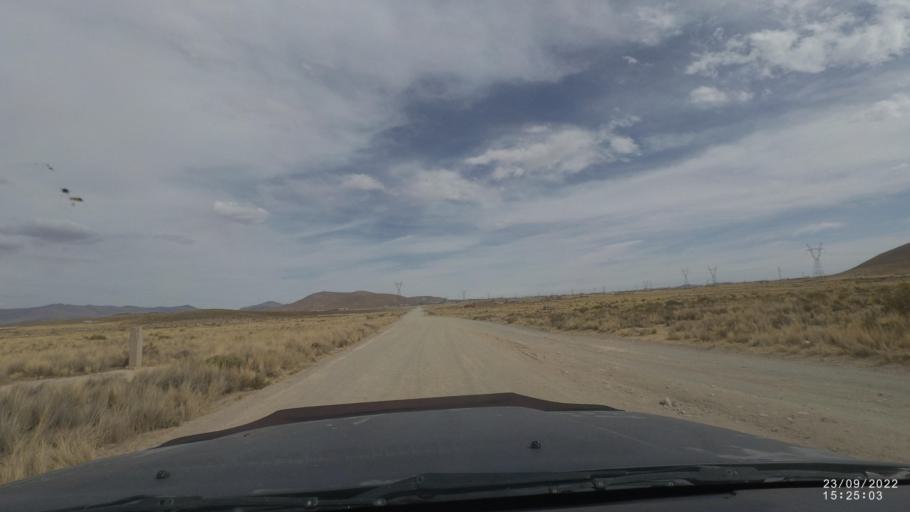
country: BO
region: Oruro
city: Oruro
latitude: -17.9412
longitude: -67.0399
